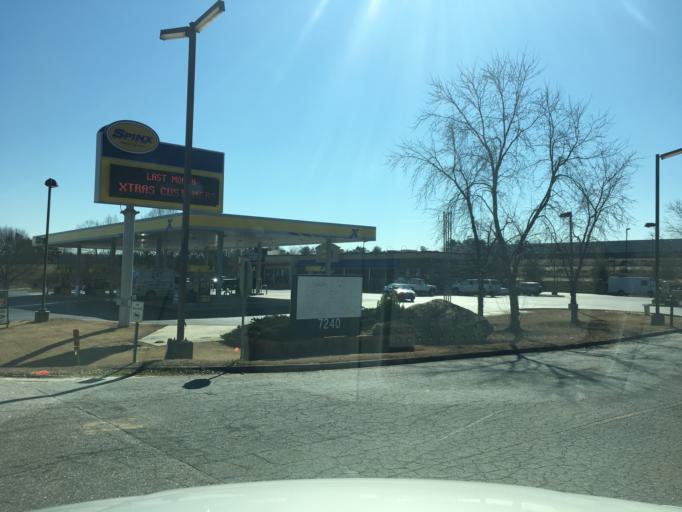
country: US
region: South Carolina
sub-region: Pickens County
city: Liberty
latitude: 34.7763
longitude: -82.6729
